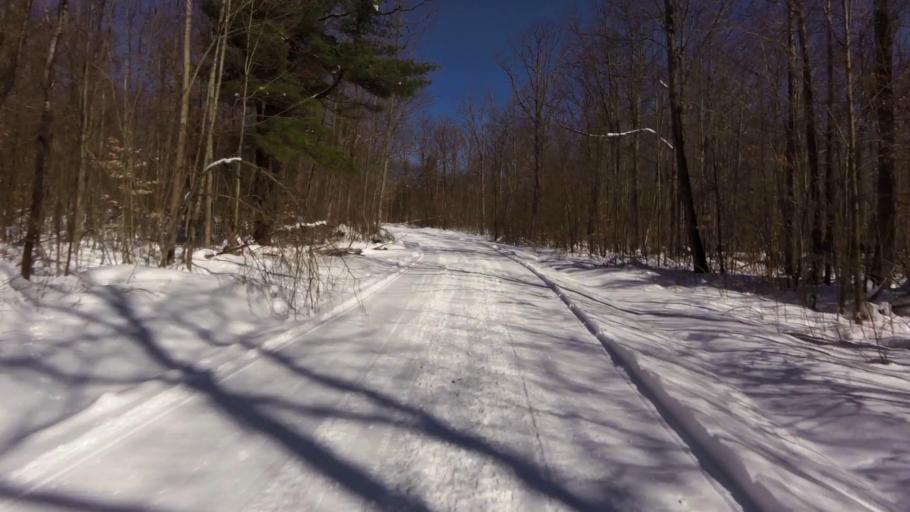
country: US
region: New York
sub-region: Allegany County
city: Houghton
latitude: 42.3350
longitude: -78.2044
